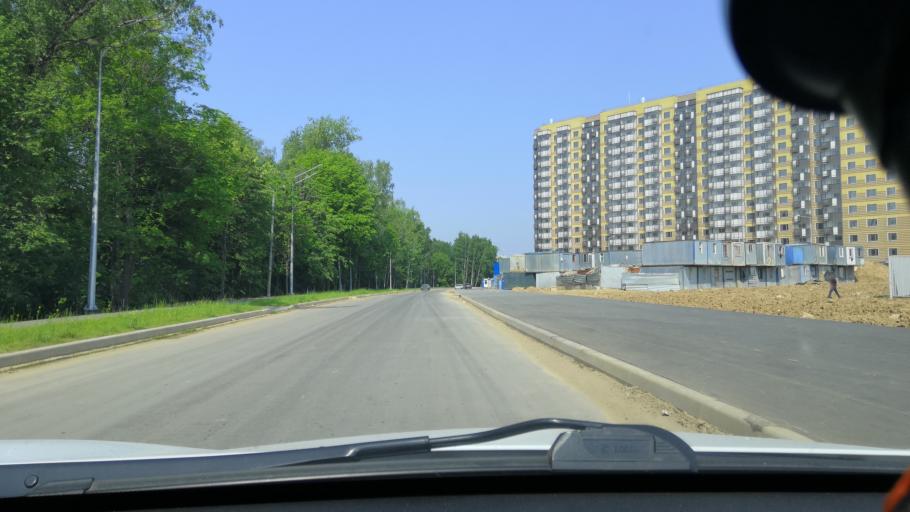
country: RU
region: Moscow
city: Severnyy
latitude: 55.9384
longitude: 37.5277
